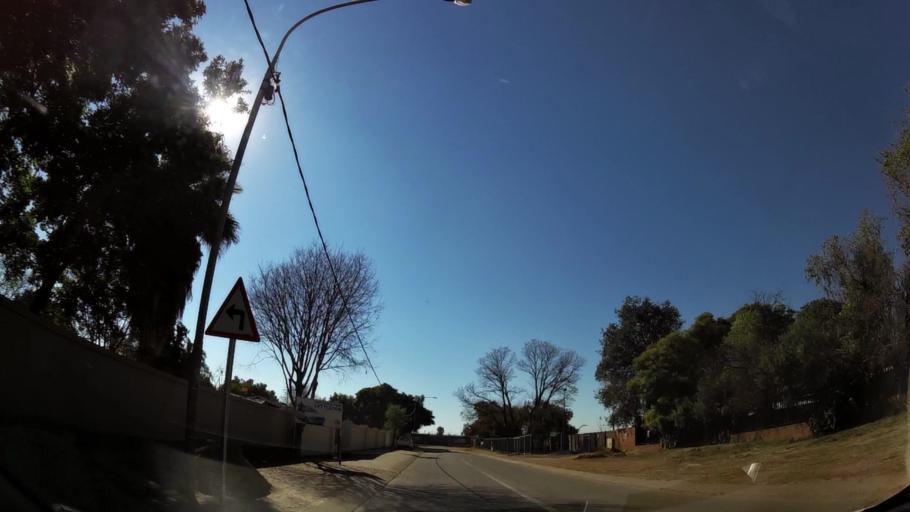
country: ZA
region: Gauteng
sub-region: City of Tshwane Metropolitan Municipality
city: Centurion
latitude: -25.8380
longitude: 28.2176
